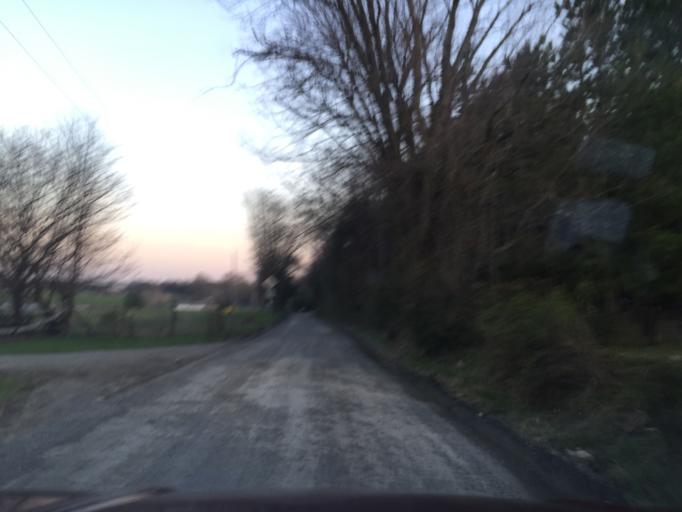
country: US
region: Maryland
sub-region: Frederick County
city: Brunswick
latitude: 39.2869
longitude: -77.5962
